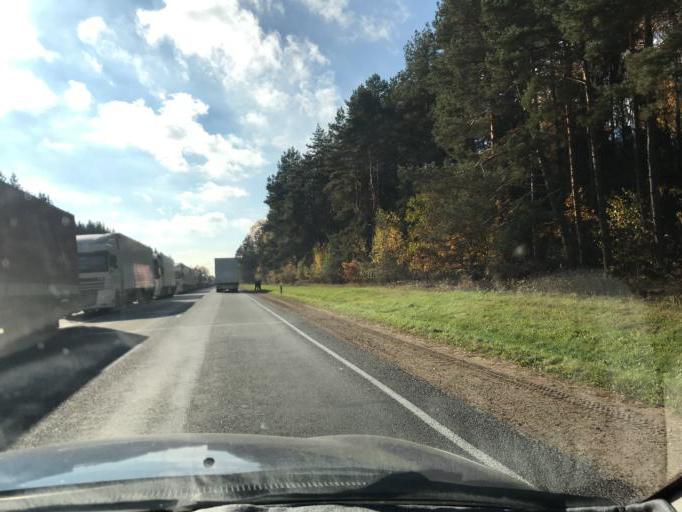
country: LT
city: Salcininkai
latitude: 54.2276
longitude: 25.3579
